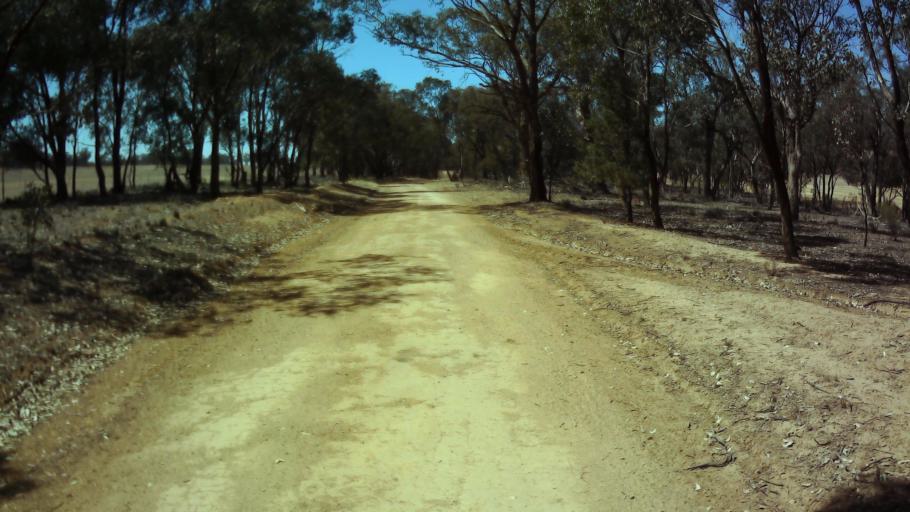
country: AU
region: New South Wales
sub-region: Weddin
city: Grenfell
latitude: -33.9579
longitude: 148.0856
